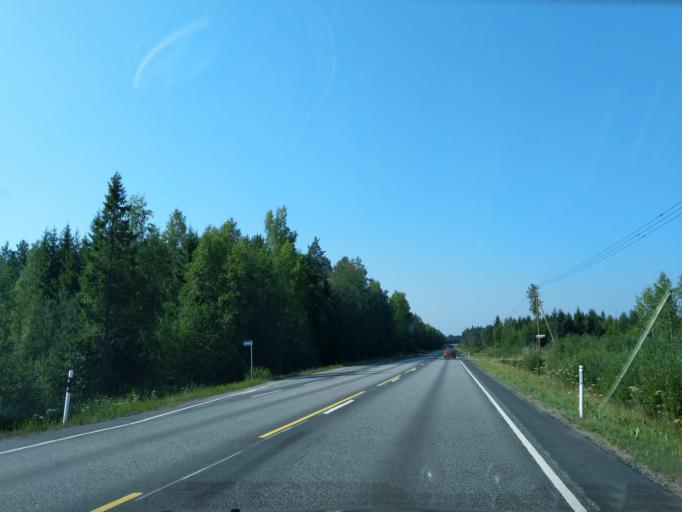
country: FI
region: Satakunta
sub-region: Pori
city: Pomarkku
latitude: 61.7189
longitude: 22.0503
